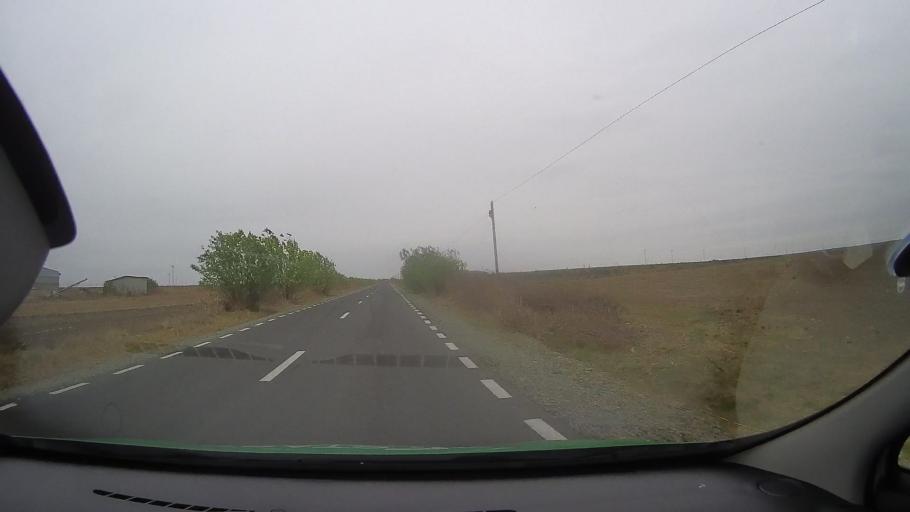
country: RO
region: Constanta
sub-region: Comuna Tortoman
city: Tortoman
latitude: 44.3645
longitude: 28.2089
